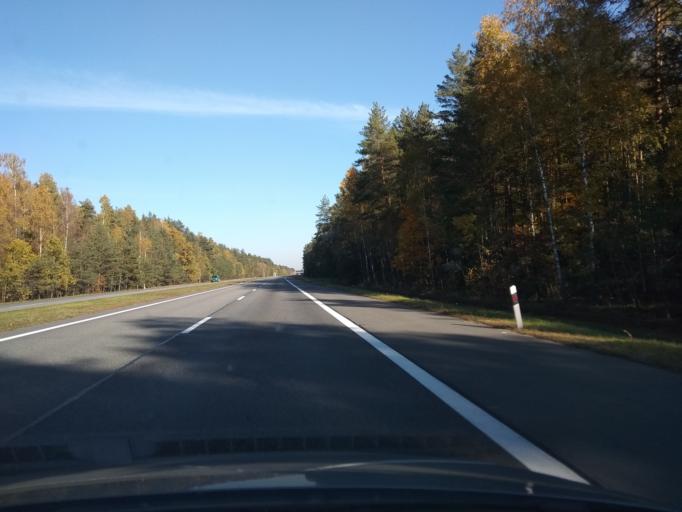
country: BY
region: Brest
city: Baranovichi
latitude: 53.0379
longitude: 25.8202
